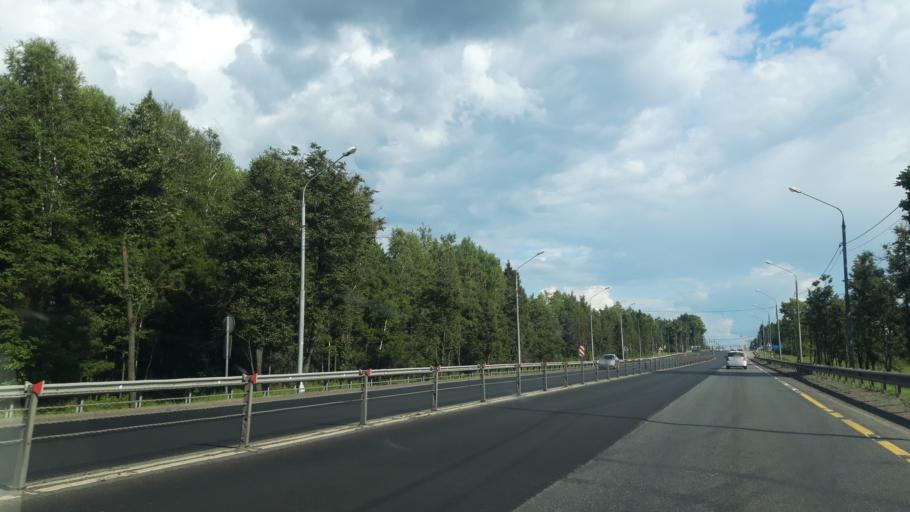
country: RU
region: Moskovskaya
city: Solnechnogorsk
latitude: 56.2545
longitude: 36.8694
